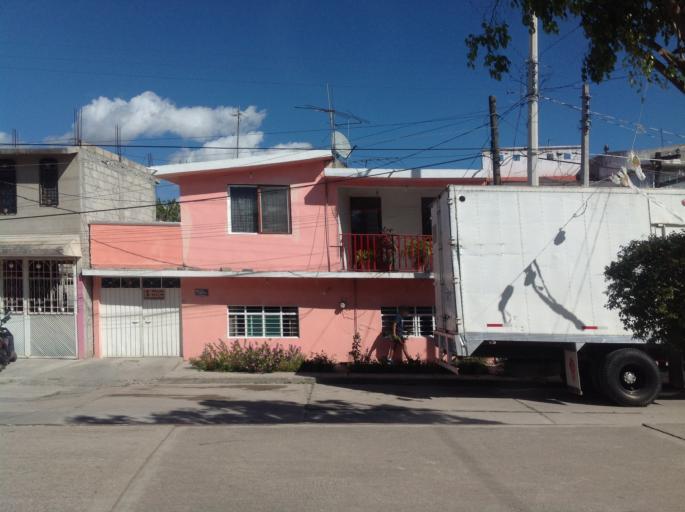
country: MX
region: Oaxaca
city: Ciudad de Huajuapam de Leon
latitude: 17.8135
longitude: -97.7656
